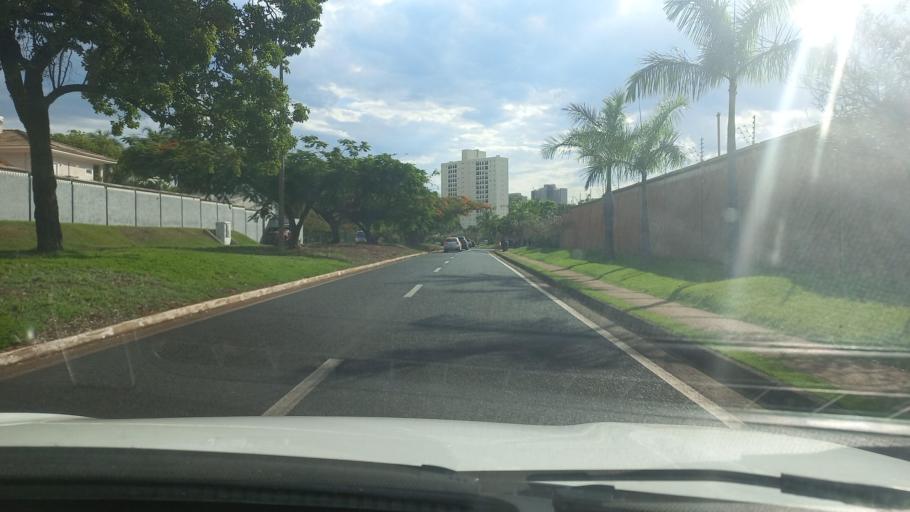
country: BR
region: Minas Gerais
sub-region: Uberaba
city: Uberaba
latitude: -19.7451
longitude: -47.9080
